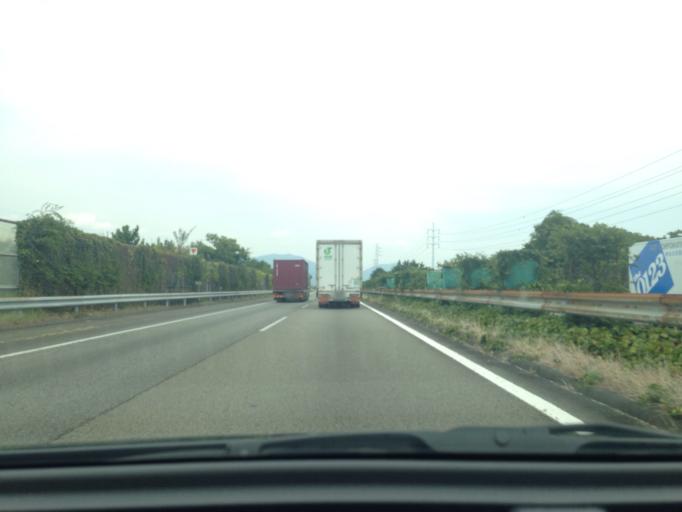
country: JP
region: Shizuoka
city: Fujieda
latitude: 34.8300
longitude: 138.2758
